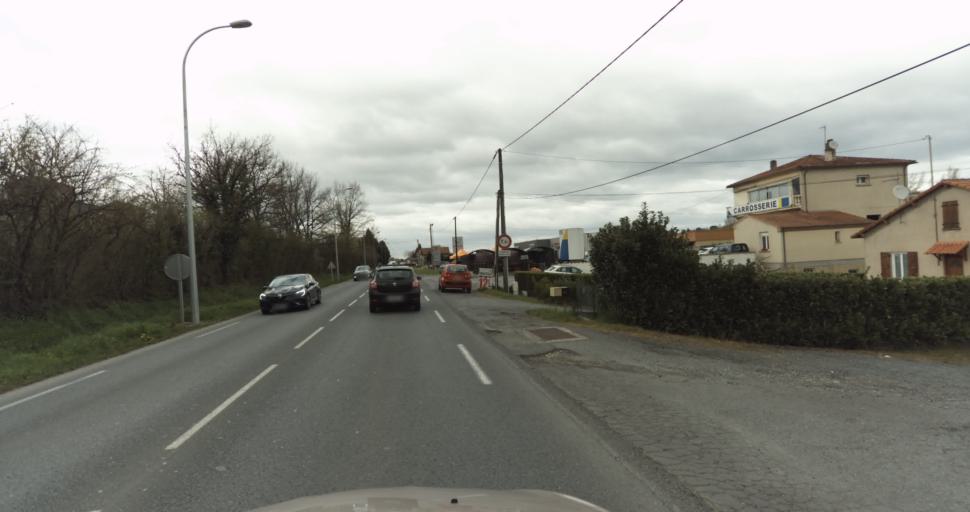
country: FR
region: Midi-Pyrenees
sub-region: Departement du Tarn
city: Puygouzon
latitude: 43.9000
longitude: 2.1477
